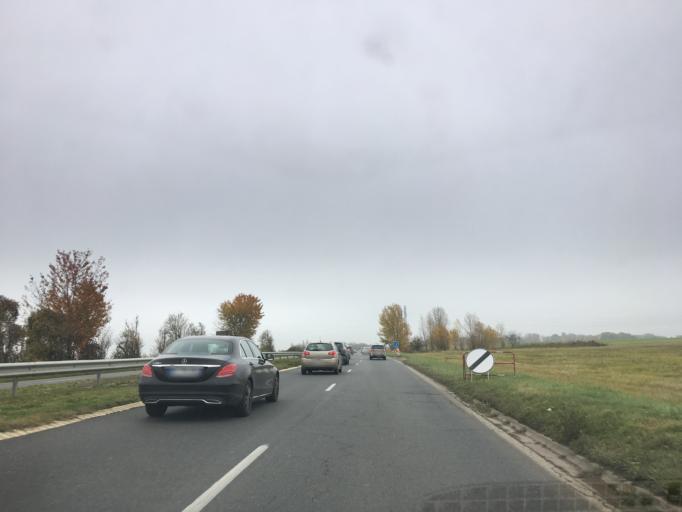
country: FR
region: Ile-de-France
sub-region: Departement de Seine-et-Marne
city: Montereau-Fault-Yonne
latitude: 48.3607
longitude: 2.9585
